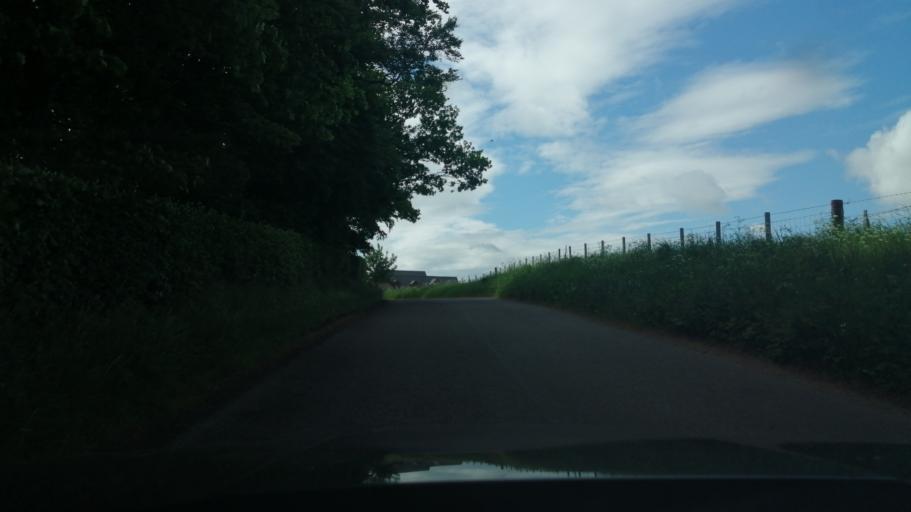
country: GB
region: Scotland
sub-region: Moray
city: Elgin
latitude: 57.6540
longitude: -3.2837
